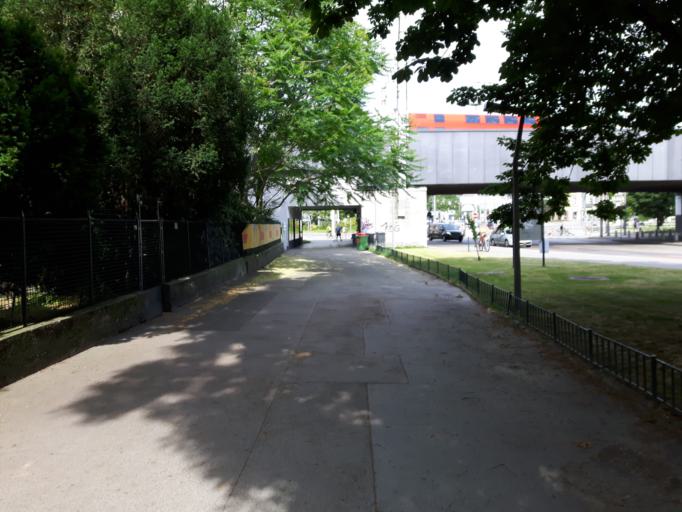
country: AT
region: Vienna
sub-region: Wien Stadt
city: Vienna
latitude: 48.2167
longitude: 16.3927
